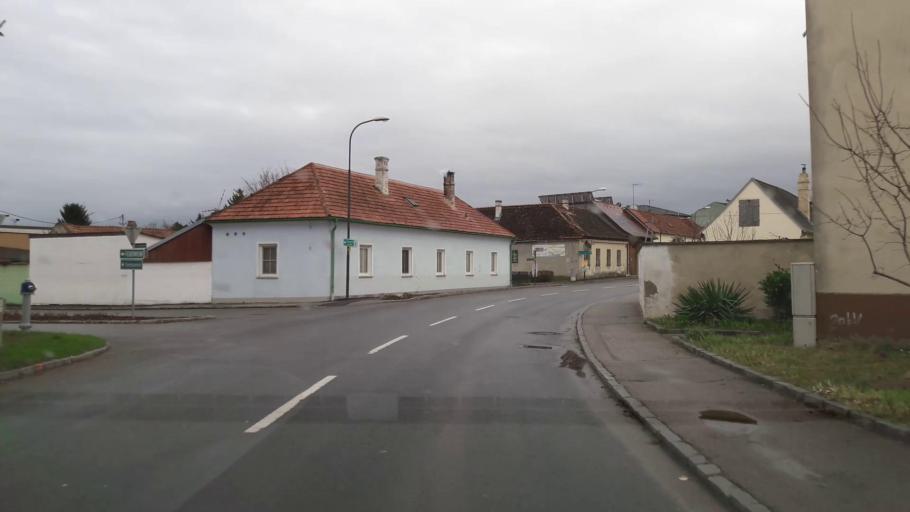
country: AT
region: Lower Austria
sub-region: Politischer Bezirk Bruck an der Leitha
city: Scharndorf
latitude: 48.0685
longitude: 16.7917
